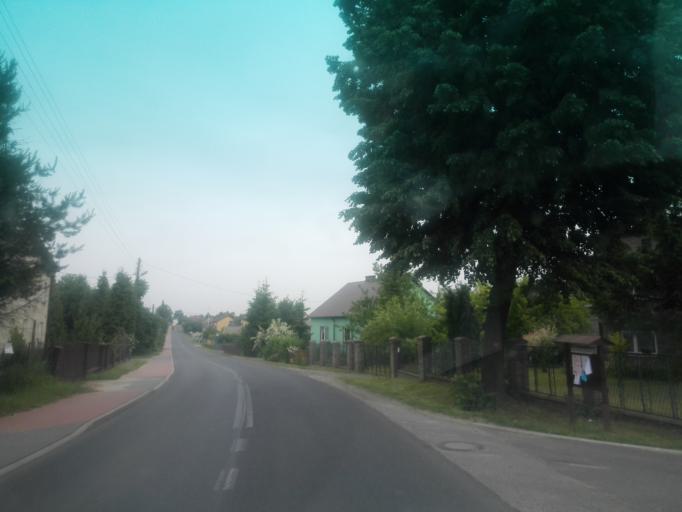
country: PL
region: Silesian Voivodeship
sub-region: Powiat czestochowski
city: Olsztyn
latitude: 50.7683
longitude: 19.2747
